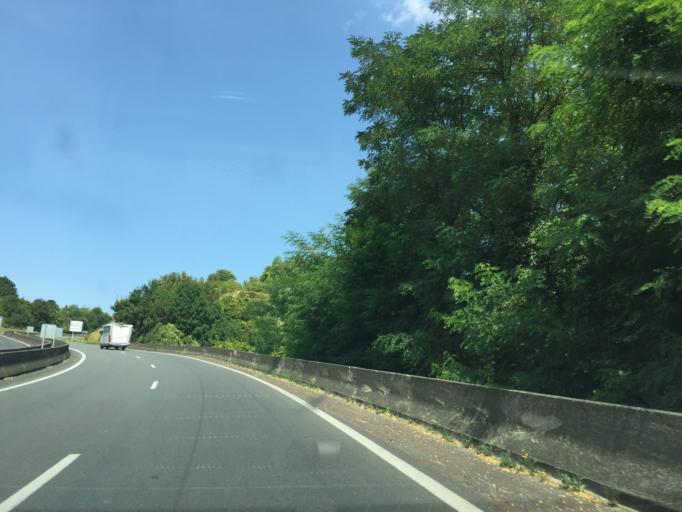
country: FR
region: Poitou-Charentes
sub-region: Departement de la Vienne
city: Biard
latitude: 46.5732
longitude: 0.3141
